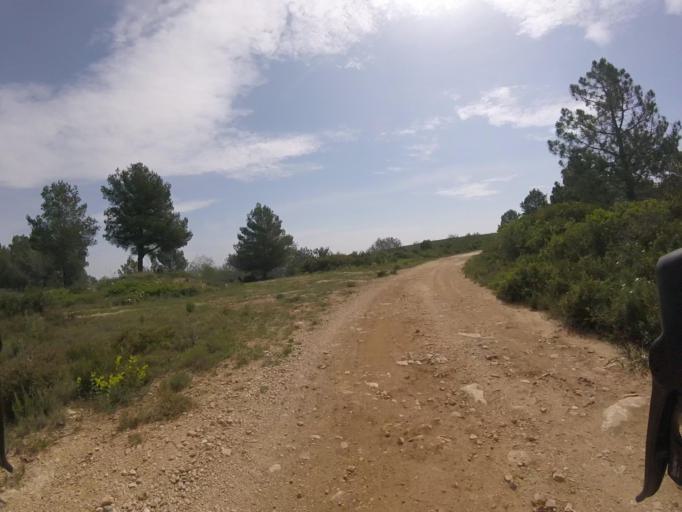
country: ES
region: Valencia
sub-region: Provincia de Castello
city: Cuevas de Vinroma
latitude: 40.2841
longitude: 0.1219
